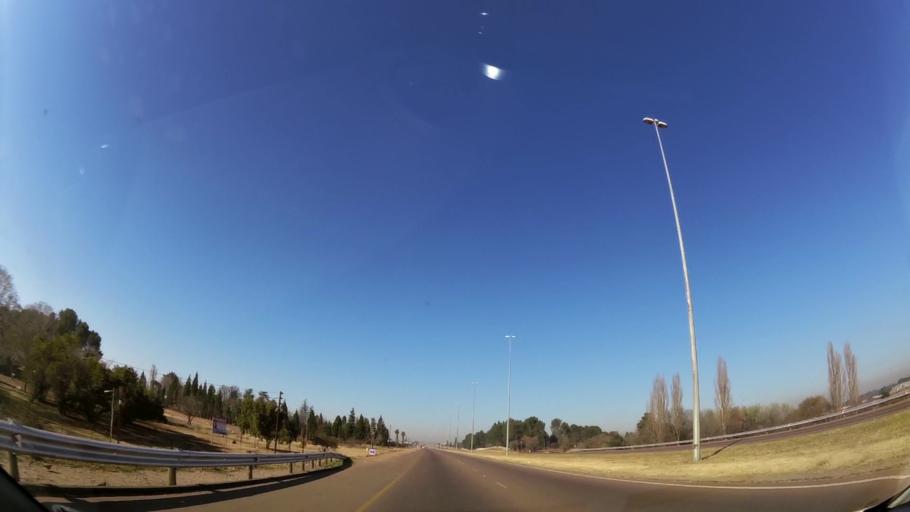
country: ZA
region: Gauteng
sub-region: City of Tshwane Metropolitan Municipality
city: Centurion
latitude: -25.8501
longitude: 28.1085
